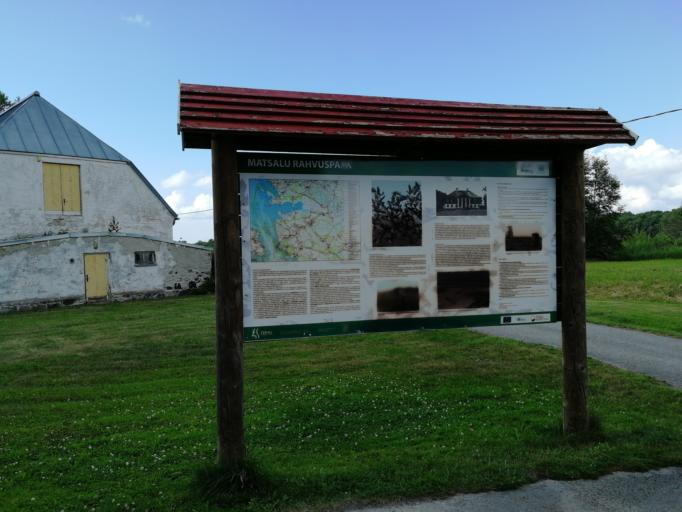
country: EE
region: Laeaene
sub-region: Lihula vald
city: Lihula
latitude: 58.7147
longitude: 23.8168
